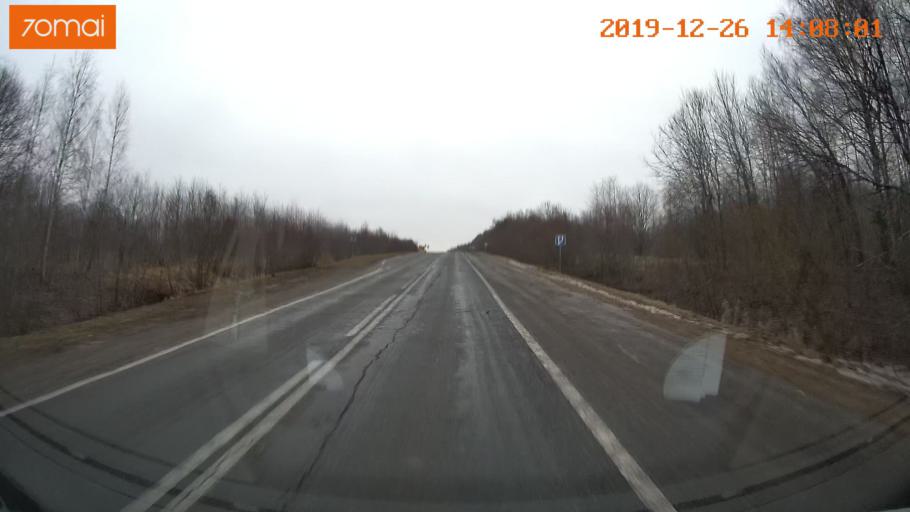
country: RU
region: Jaroslavl
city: Poshekhon'ye
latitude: 58.5089
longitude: 38.9028
